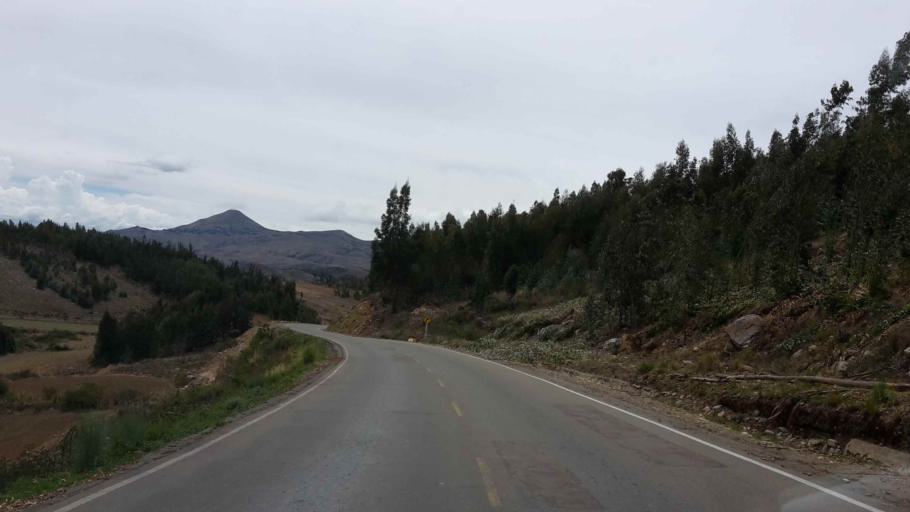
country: BO
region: Cochabamba
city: Arani
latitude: -17.4607
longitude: -65.7044
